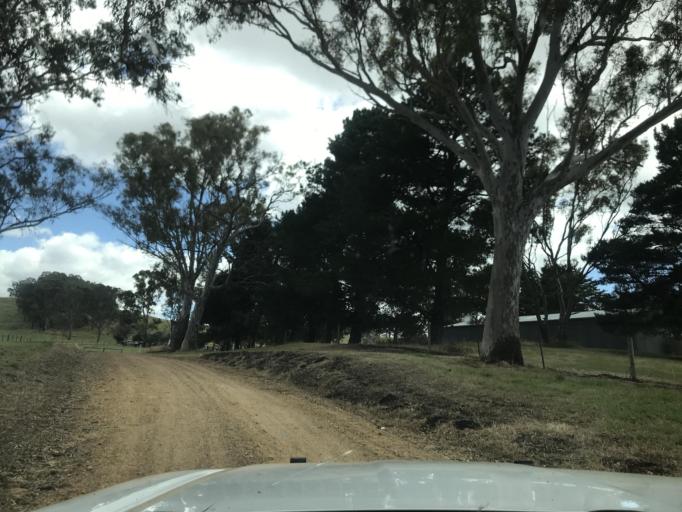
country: AU
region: South Australia
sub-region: Wattle Range
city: Penola
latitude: -37.3666
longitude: 141.2445
